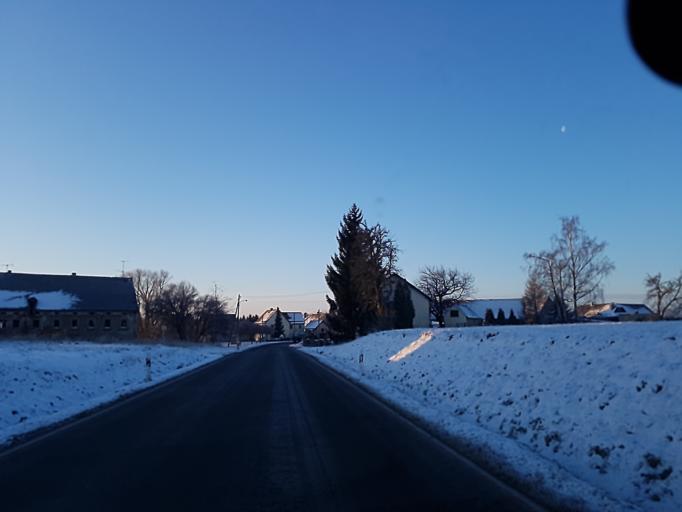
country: DE
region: Saxony
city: Grossweitzschen
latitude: 51.1757
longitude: 13.0441
